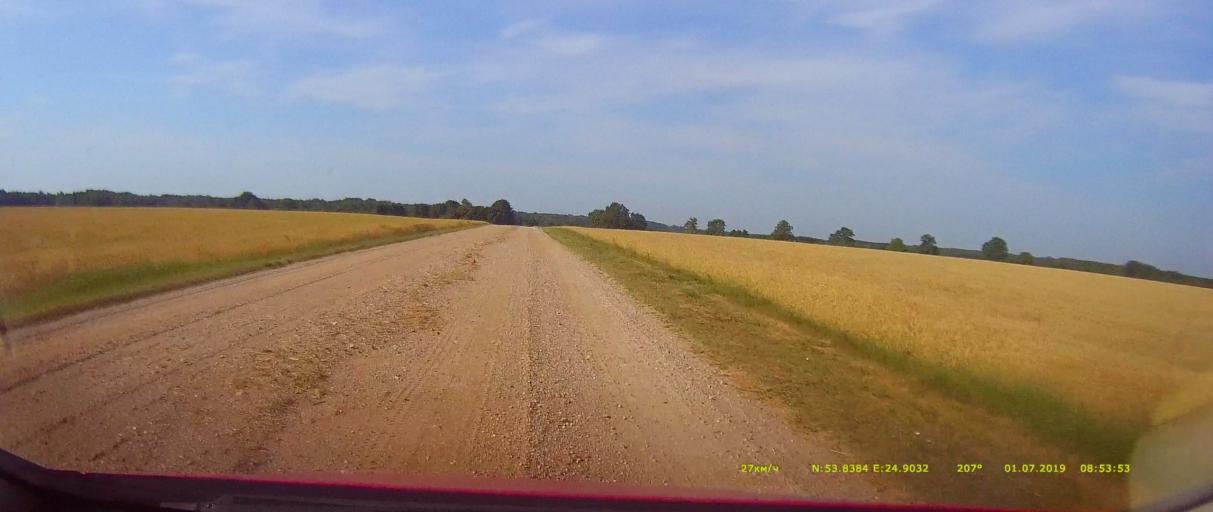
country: BY
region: Grodnenskaya
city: Shchuchin
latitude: 53.8385
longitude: 24.9033
